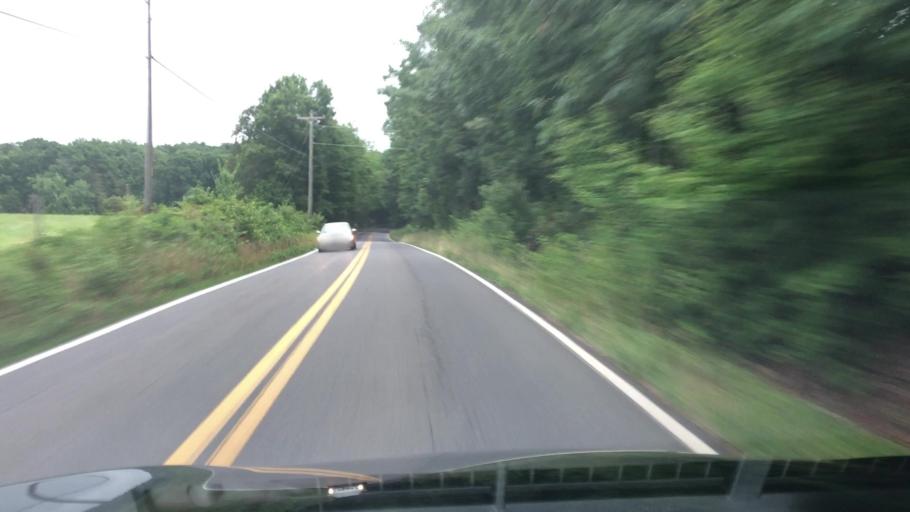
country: US
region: Virginia
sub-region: Fauquier County
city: Bealeton
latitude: 38.5164
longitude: -77.6075
